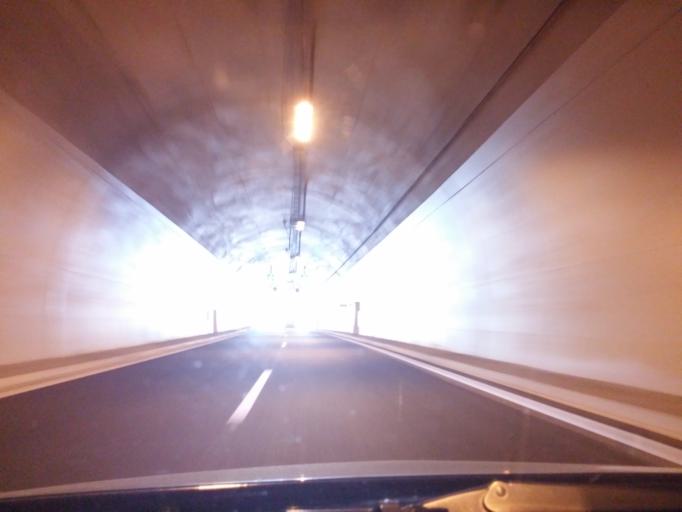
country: GR
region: Peloponnese
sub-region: Nomos Korinthias
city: Nemea
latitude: 37.6934
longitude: 22.5260
